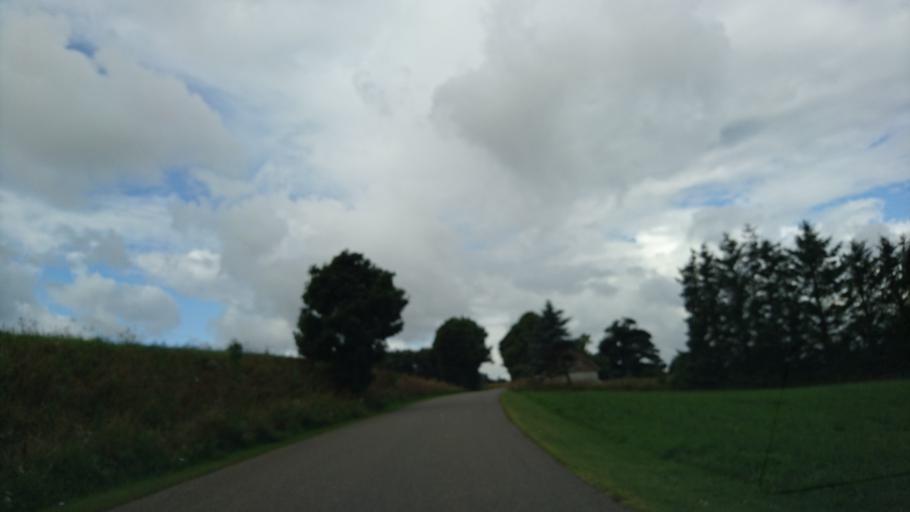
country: DK
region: North Denmark
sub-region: Hjorring Kommune
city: Tars
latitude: 57.3688
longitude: 10.2073
